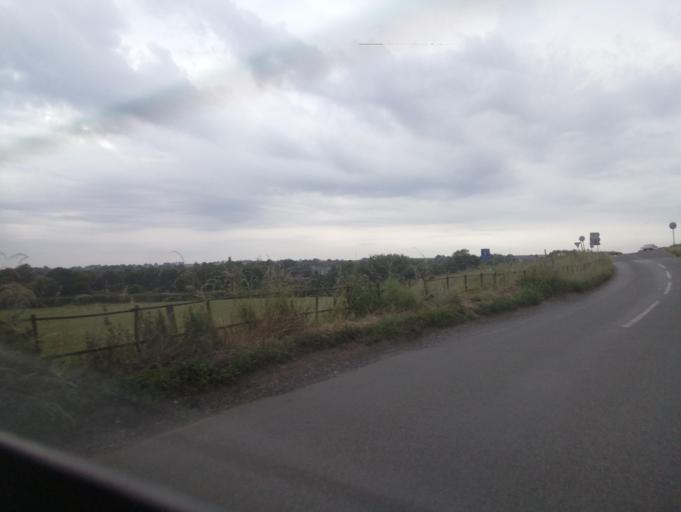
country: GB
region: England
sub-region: Dorset
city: Sherborne
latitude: 50.9381
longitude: -2.5181
